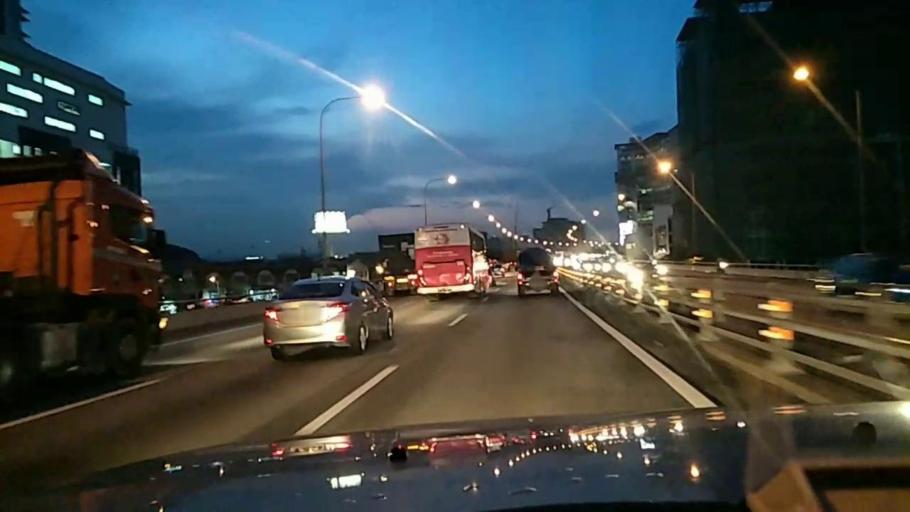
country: MY
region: Selangor
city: Shah Alam
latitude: 3.0751
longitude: 101.5526
